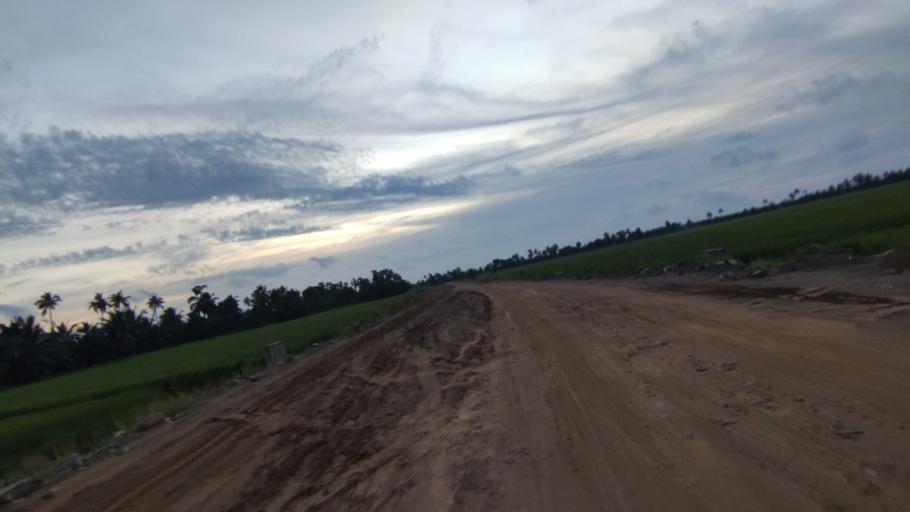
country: IN
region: Kerala
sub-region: Kottayam
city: Kottayam
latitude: 9.6469
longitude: 76.4631
